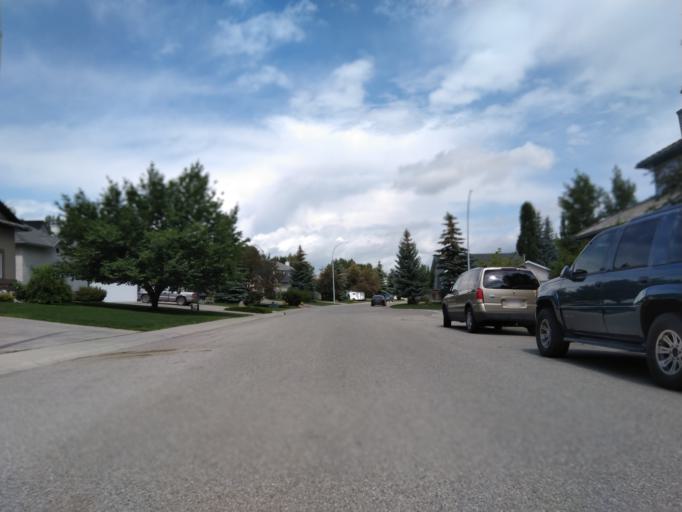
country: CA
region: Alberta
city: Cochrane
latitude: 51.1857
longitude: -114.4990
